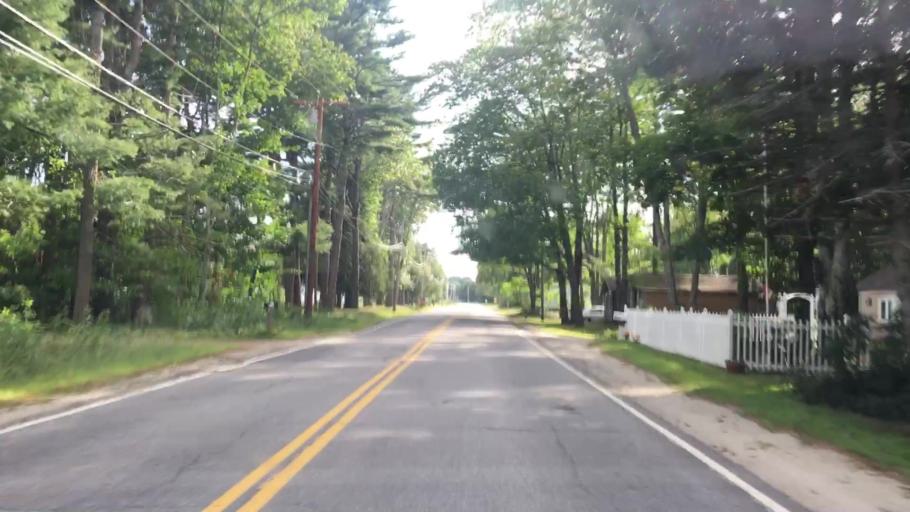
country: US
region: Maine
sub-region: Sagadahoc County
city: Bath
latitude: 43.9281
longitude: -69.8922
